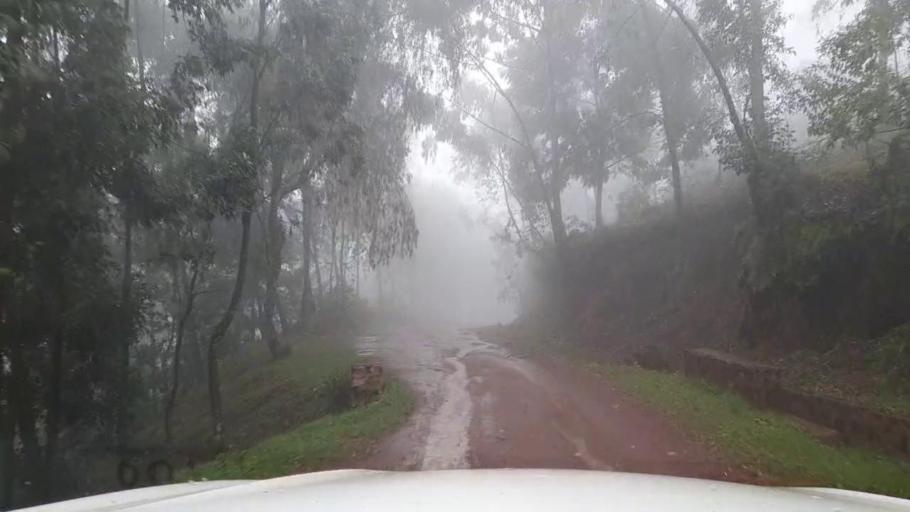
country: RW
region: Kigali
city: Kigali
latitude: -1.7687
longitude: 29.9961
